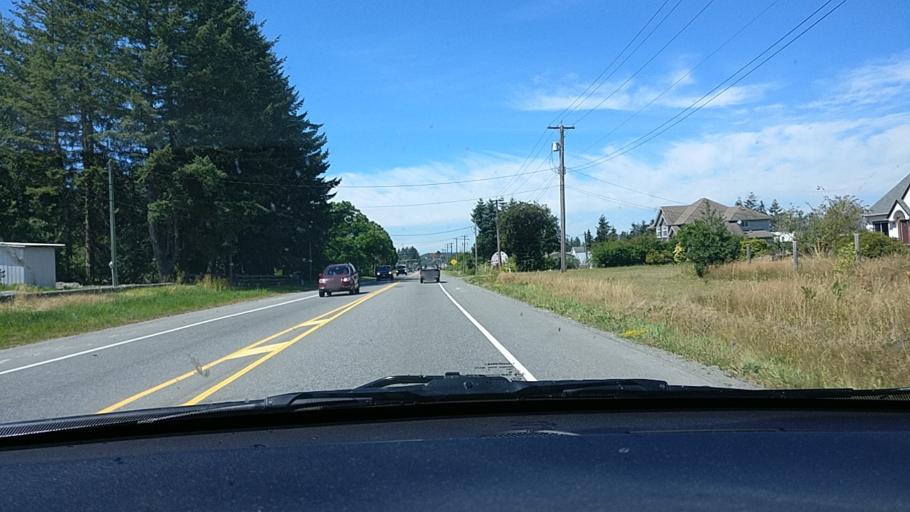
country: CA
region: British Columbia
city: Aldergrove
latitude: 49.0573
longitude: -122.4424
